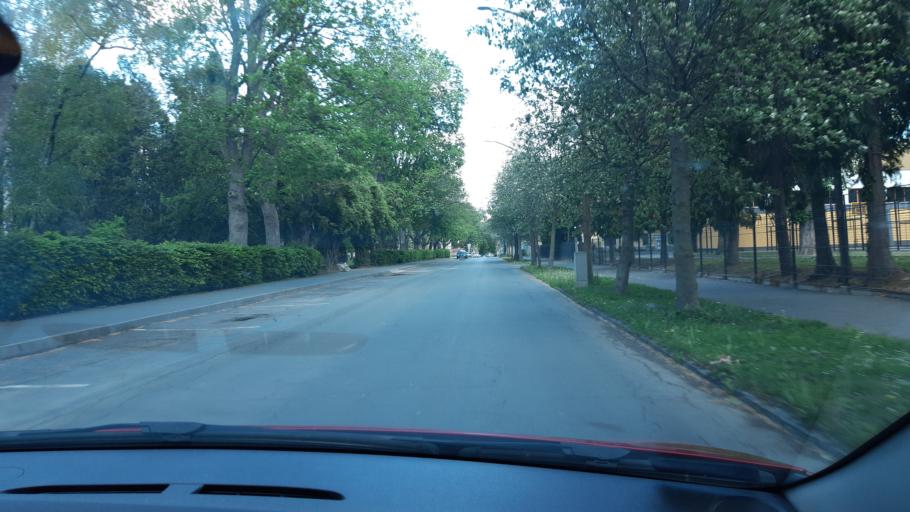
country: HU
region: Somogy
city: Kaposvar
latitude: 46.3621
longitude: 17.7917
